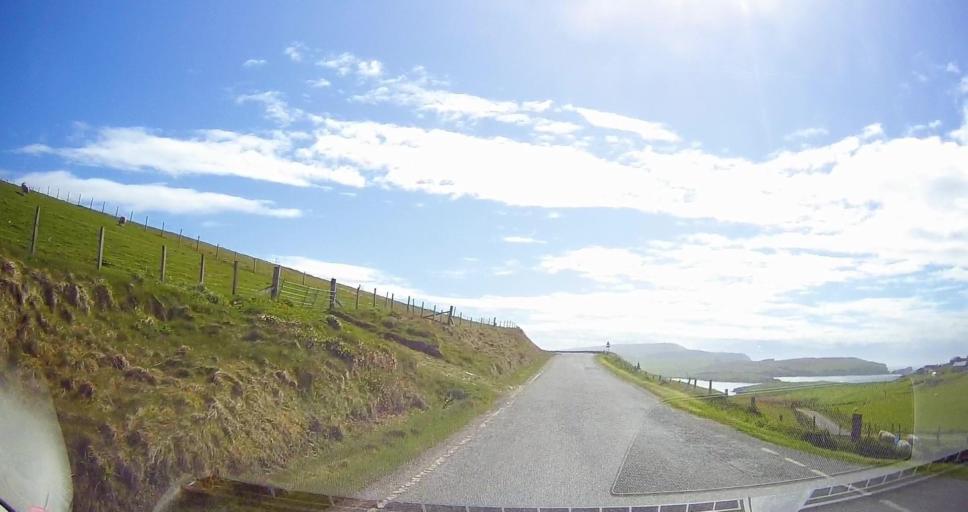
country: GB
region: Scotland
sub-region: Shetland Islands
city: Sandwick
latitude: 59.9609
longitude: -1.3238
